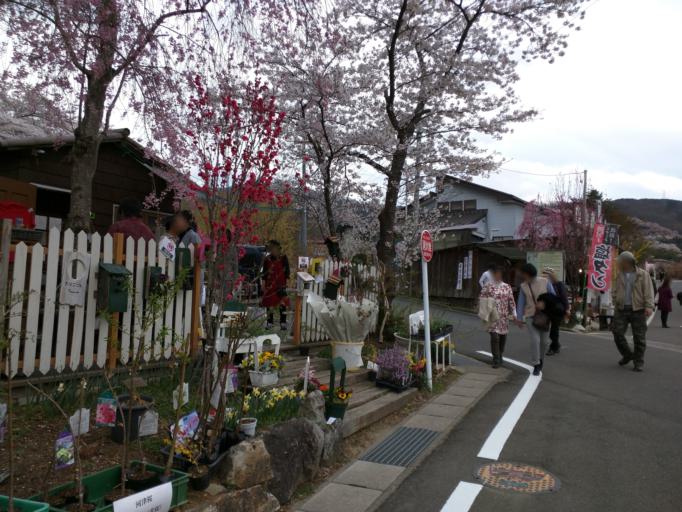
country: JP
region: Fukushima
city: Fukushima-shi
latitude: 37.7438
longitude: 140.4921
